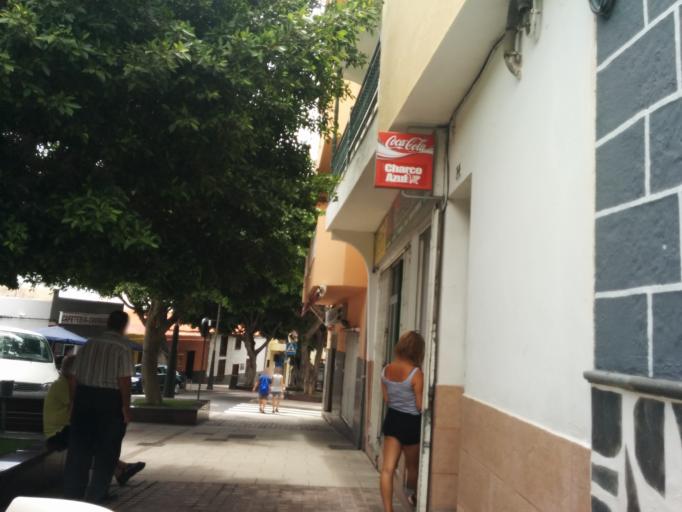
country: ES
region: Canary Islands
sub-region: Provincia de Santa Cruz de Tenerife
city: Adeje
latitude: 28.1222
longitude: -16.7246
